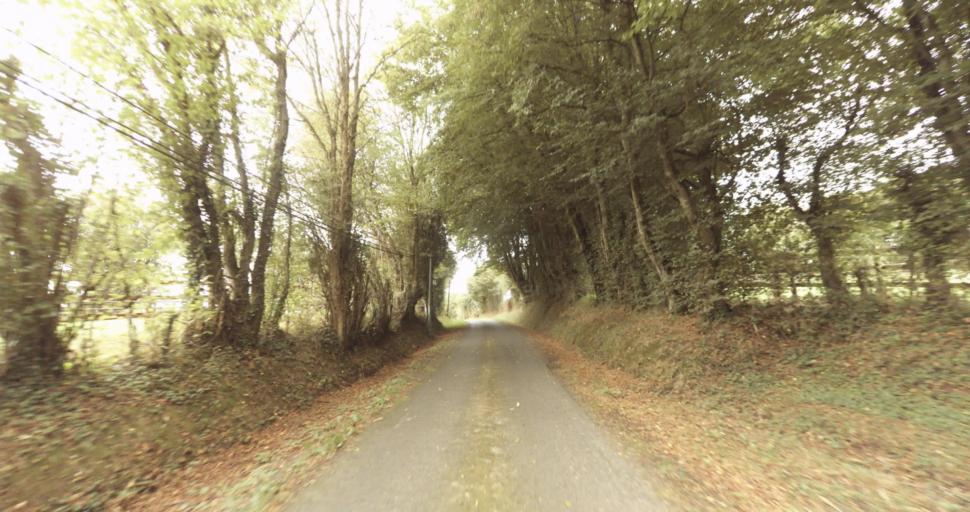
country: FR
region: Lower Normandy
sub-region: Departement de l'Orne
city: Gace
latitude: 48.7302
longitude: 0.2929
